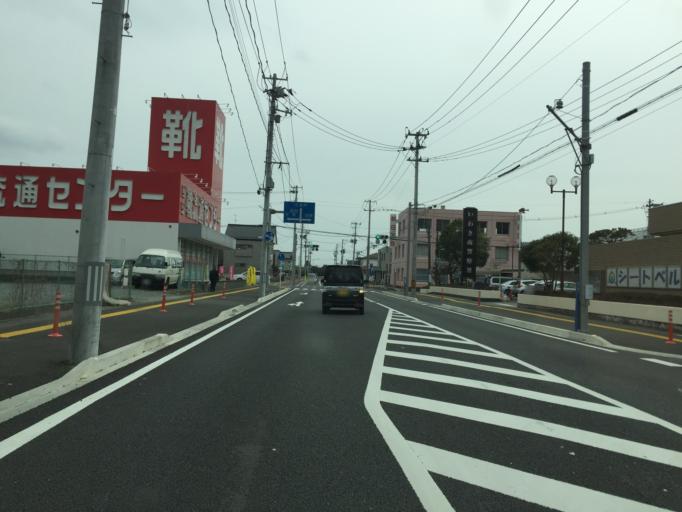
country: JP
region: Ibaraki
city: Kitaibaraki
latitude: 36.9169
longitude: 140.8006
